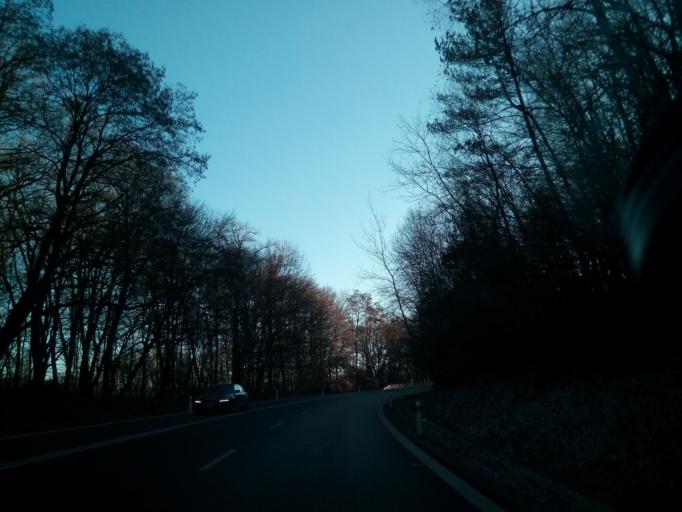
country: SK
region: Kosicky
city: Kosice
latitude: 48.7358
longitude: 21.3759
